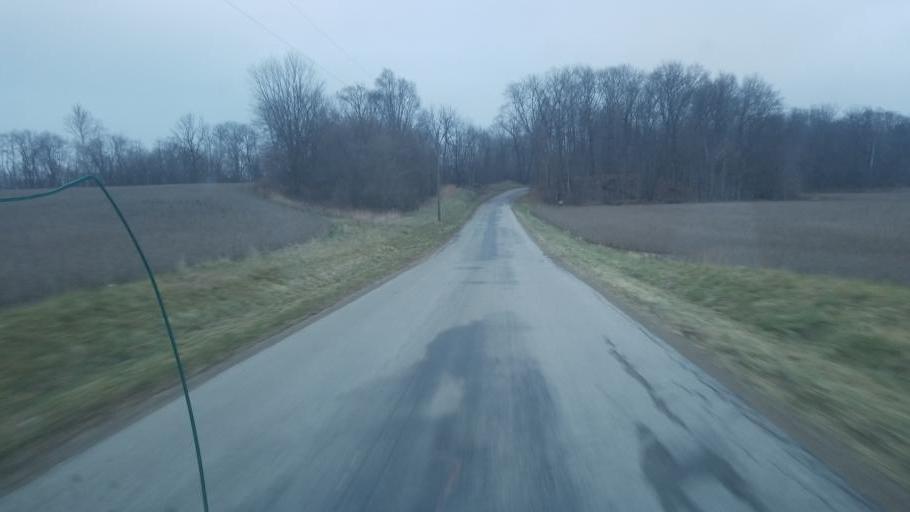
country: US
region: Ohio
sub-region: Seneca County
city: Tiffin
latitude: 40.9876
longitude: -83.1974
